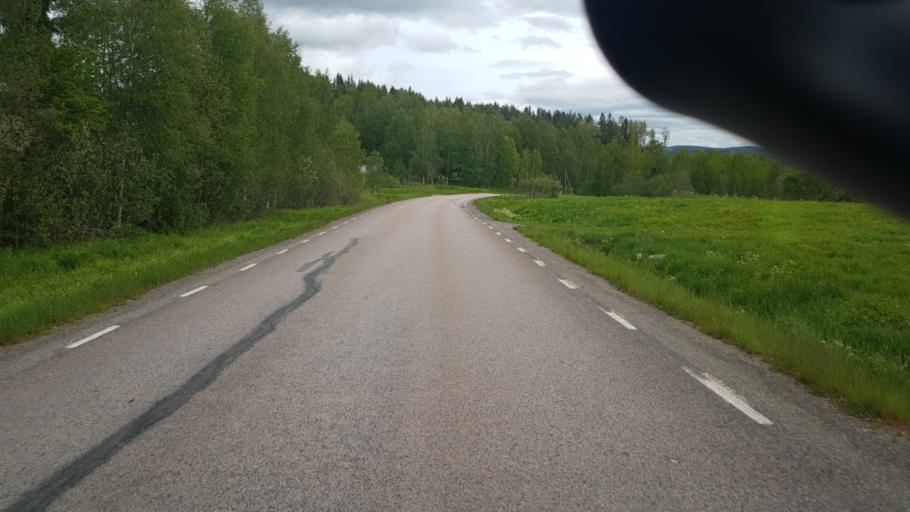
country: SE
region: Vaermland
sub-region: Eda Kommun
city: Amotfors
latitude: 59.8723
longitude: 12.5039
